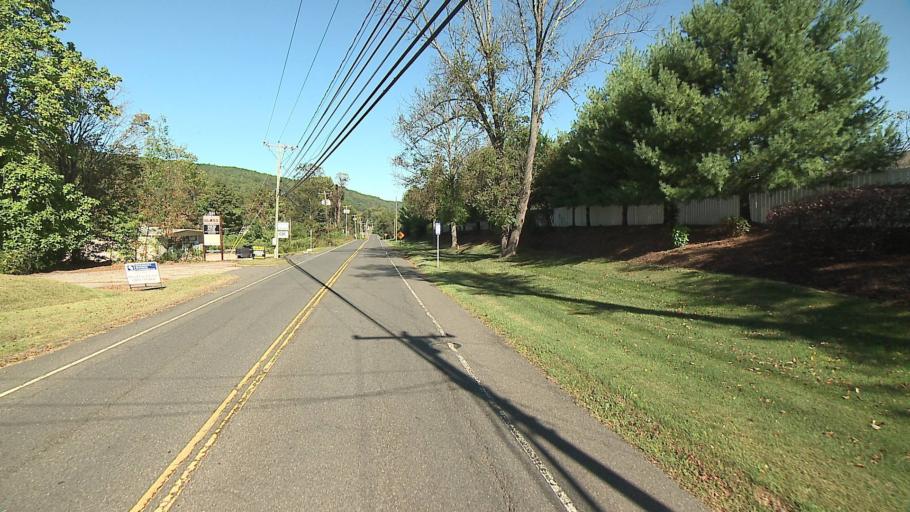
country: US
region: Connecticut
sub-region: Litchfield County
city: New Milford
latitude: 41.4894
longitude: -73.4138
